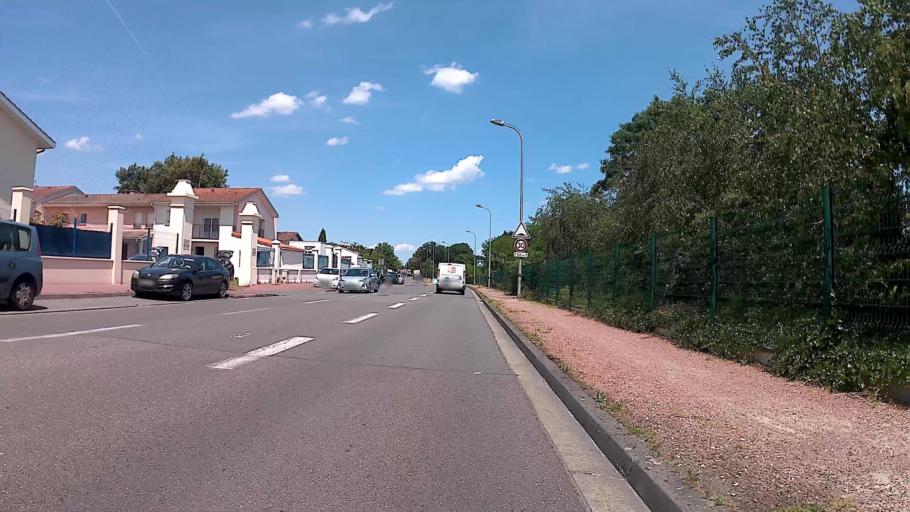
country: FR
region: Aquitaine
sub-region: Departement de la Gironde
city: Talence
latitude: 44.7968
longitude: -0.5781
